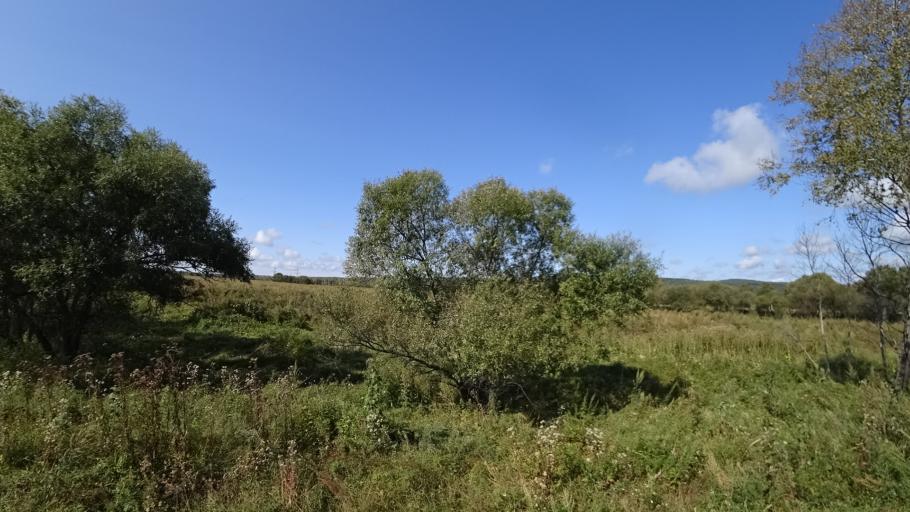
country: RU
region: Amur
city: Arkhara
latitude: 49.4130
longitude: 130.1700
